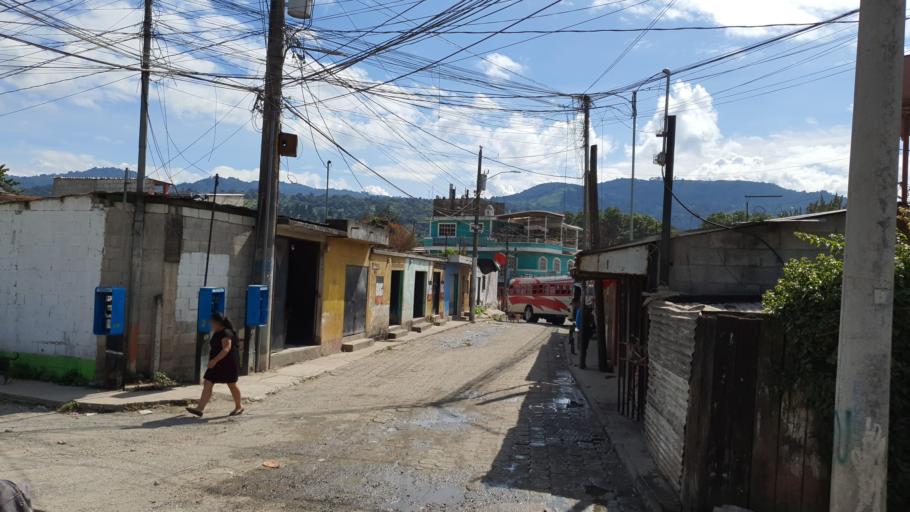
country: GT
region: Guatemala
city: Villa Canales
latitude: 14.4776
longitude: -90.5379
